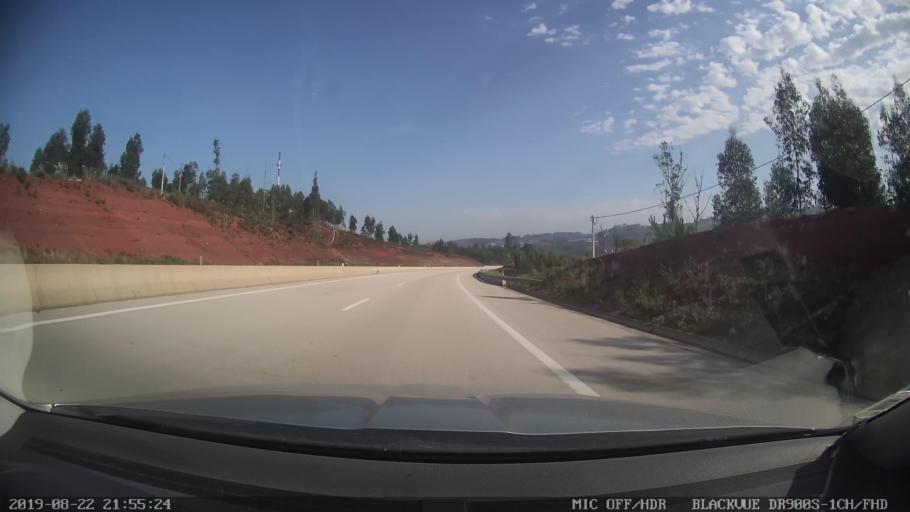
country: PT
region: Coimbra
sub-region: Coimbra
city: Coimbra
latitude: 40.1529
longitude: -8.3849
